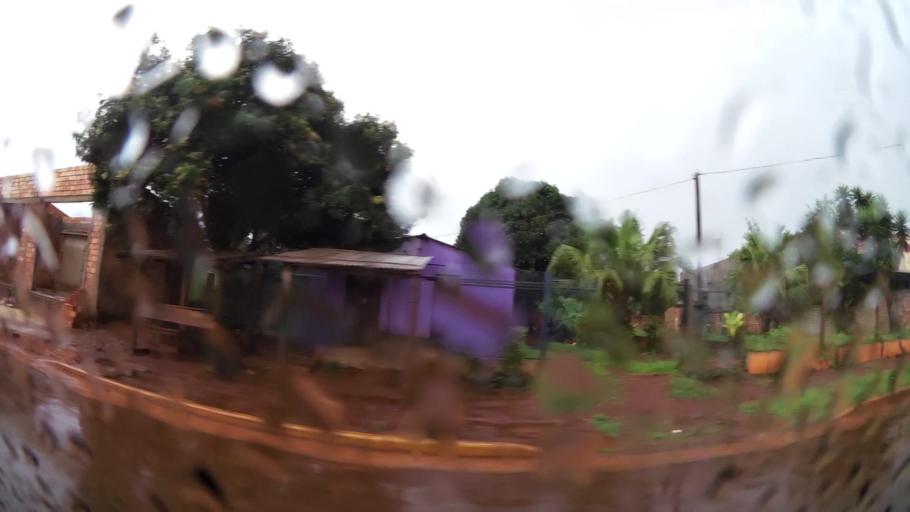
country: PY
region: Alto Parana
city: Presidente Franco
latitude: -25.5486
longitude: -54.6728
